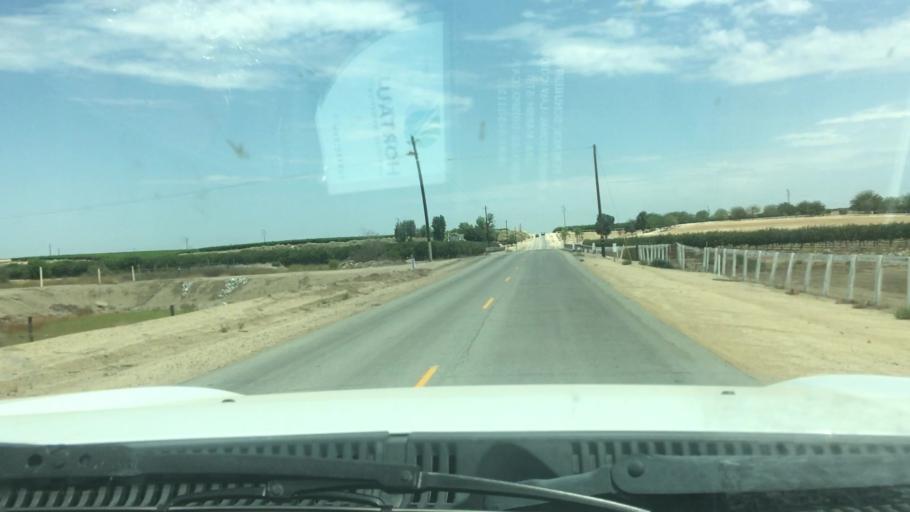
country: US
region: California
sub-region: Kern County
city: Shafter
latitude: 35.5617
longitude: -119.1512
